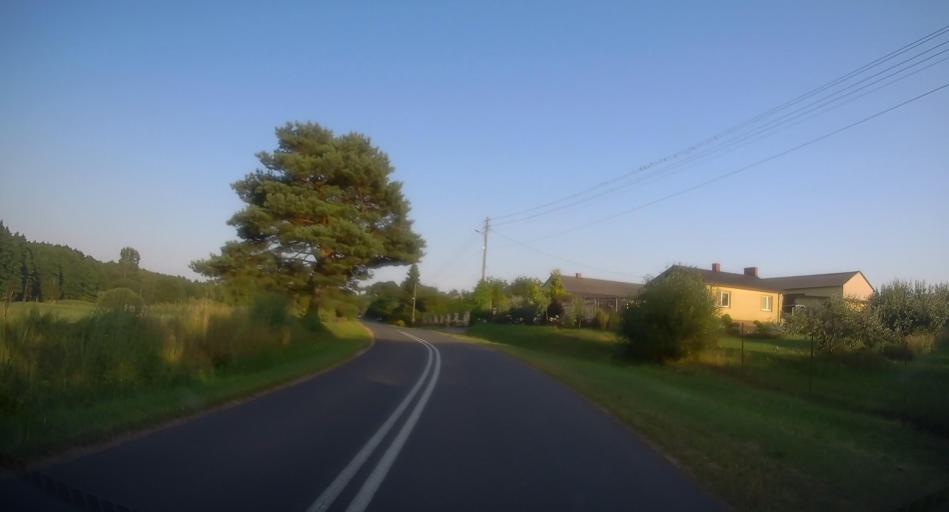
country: PL
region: Lodz Voivodeship
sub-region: Powiat skierniewicki
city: Kowiesy
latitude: 51.8952
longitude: 20.3806
